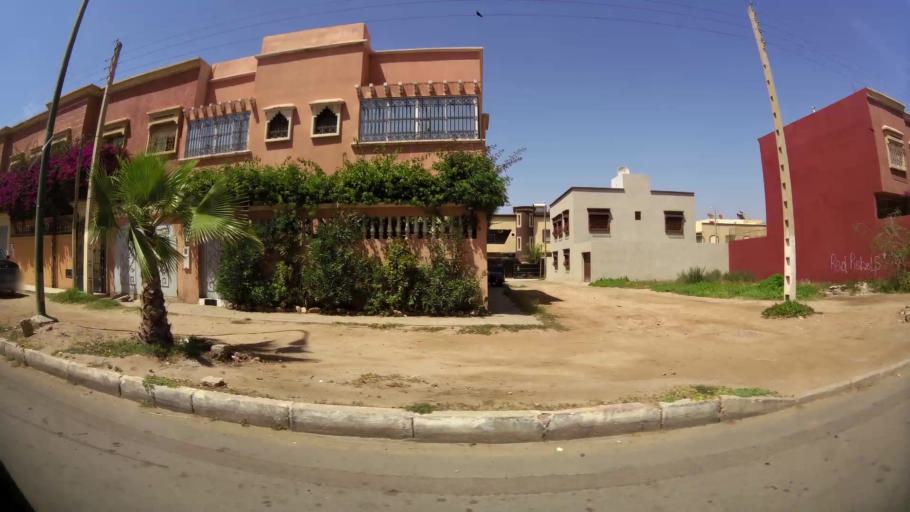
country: MA
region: Souss-Massa-Draa
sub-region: Inezgane-Ait Mellou
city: Inezgane
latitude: 30.3488
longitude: -9.5075
